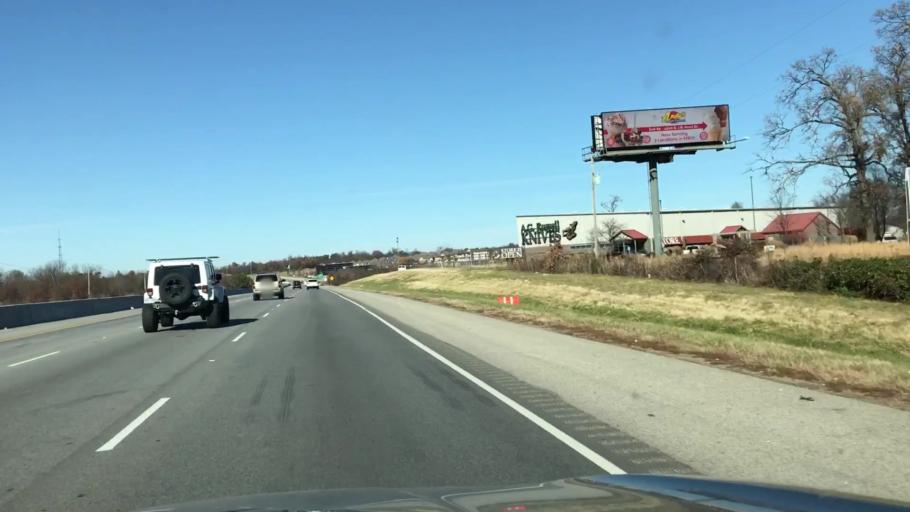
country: US
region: Arkansas
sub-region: Benton County
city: Lowell
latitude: 36.2883
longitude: -94.1601
